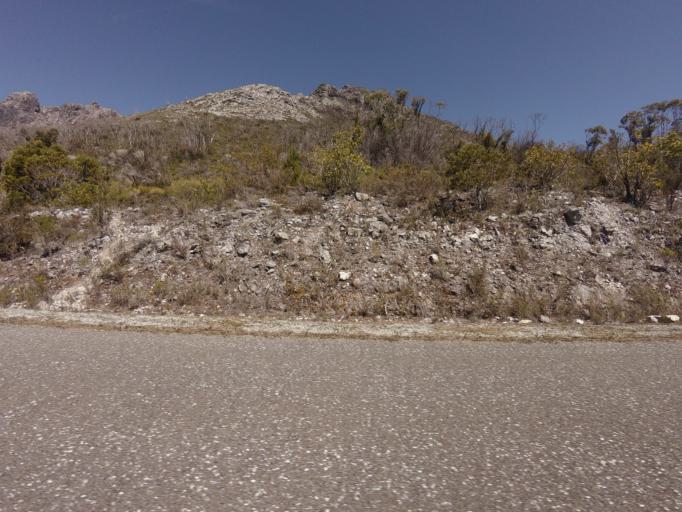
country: AU
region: Tasmania
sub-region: Huon Valley
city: Geeveston
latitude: -42.8616
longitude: 146.2229
